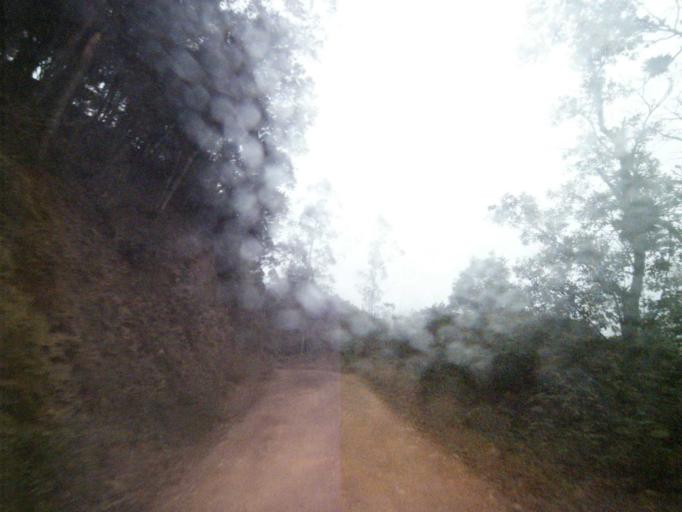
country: BR
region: Santa Catarina
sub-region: Anitapolis
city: Anitapolis
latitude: -27.8802
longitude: -49.1330
